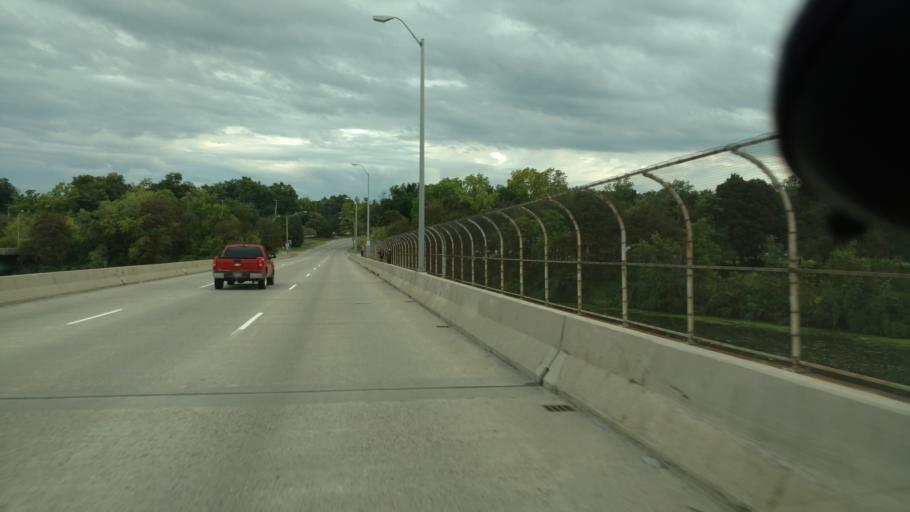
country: US
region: Michigan
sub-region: Ingham County
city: Lansing
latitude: 42.7207
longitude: -84.5690
